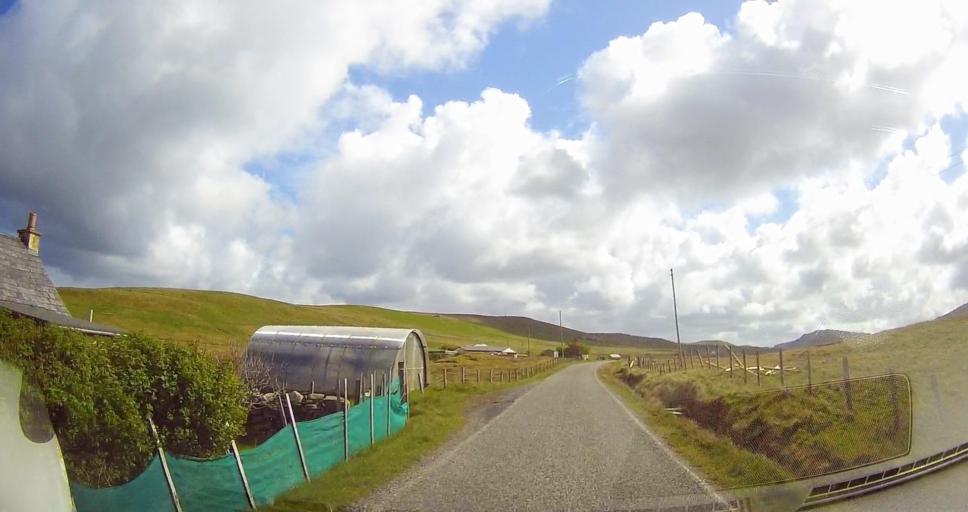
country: GB
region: Scotland
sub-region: Shetland Islands
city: Lerwick
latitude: 60.5766
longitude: -1.3312
